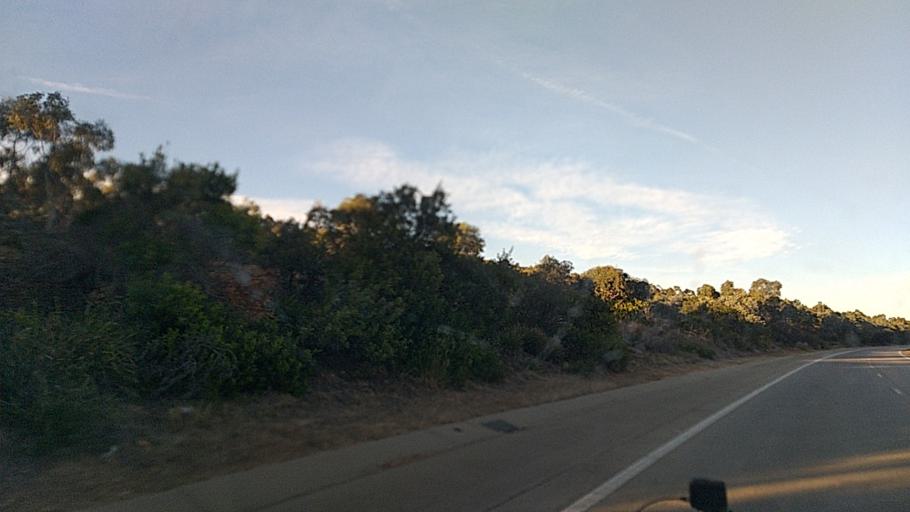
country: AU
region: New South Wales
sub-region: Yass Valley
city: Gundaroo
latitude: -35.1073
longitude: 149.3710
